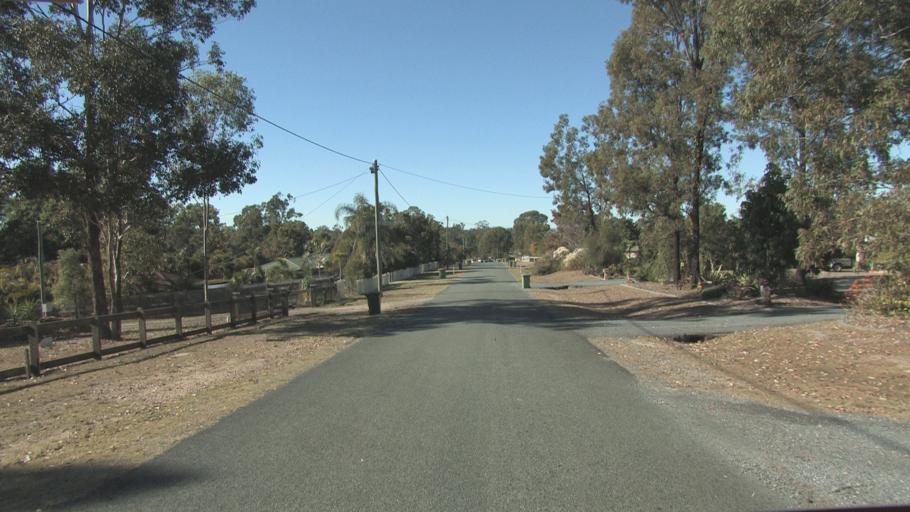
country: AU
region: Queensland
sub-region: Logan
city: North Maclean
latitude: -27.7406
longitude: 152.9658
